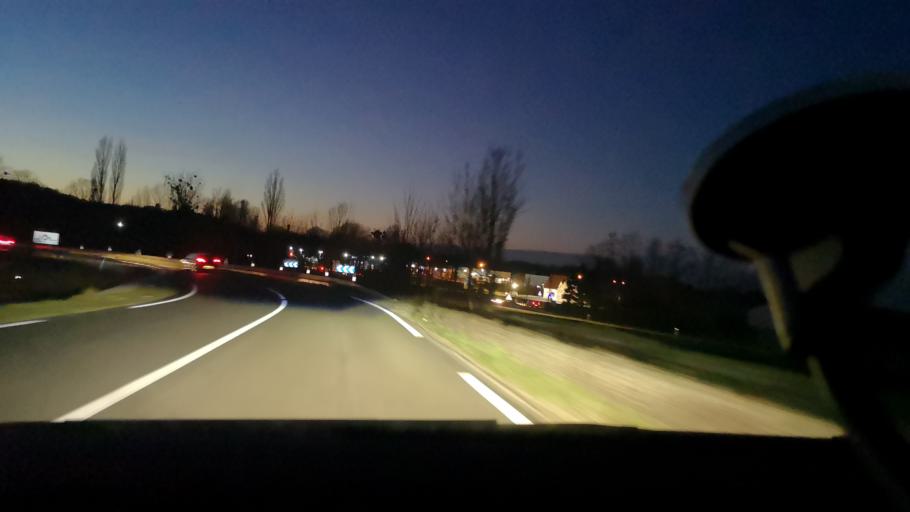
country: FR
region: Franche-Comte
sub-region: Departement du Jura
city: Poligny
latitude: 46.8362
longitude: 5.6928
